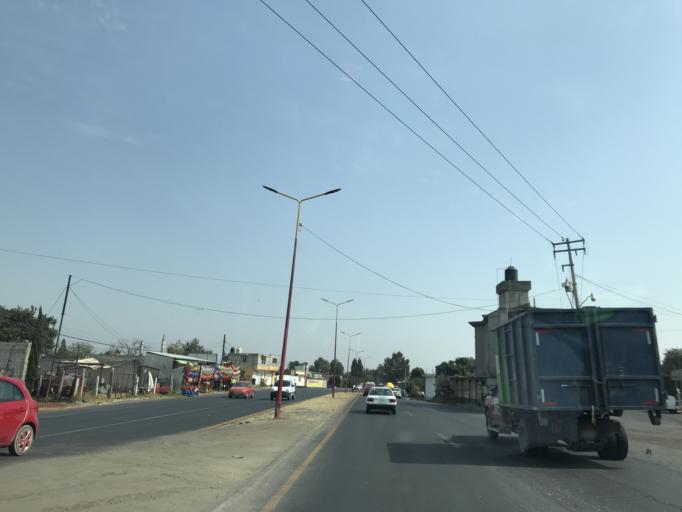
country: MX
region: Tlaxcala
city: La Magdalena Tlaltelulco
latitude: 19.2707
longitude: -98.1975
